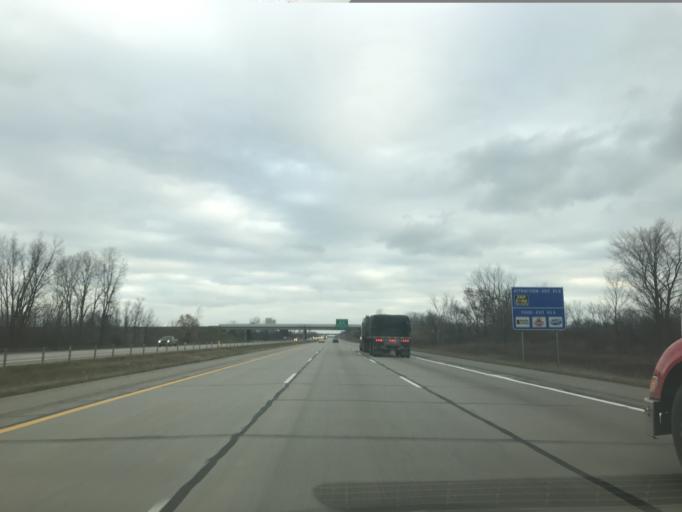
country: US
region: Michigan
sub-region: Eaton County
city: Waverly
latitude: 42.7173
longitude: -84.6690
